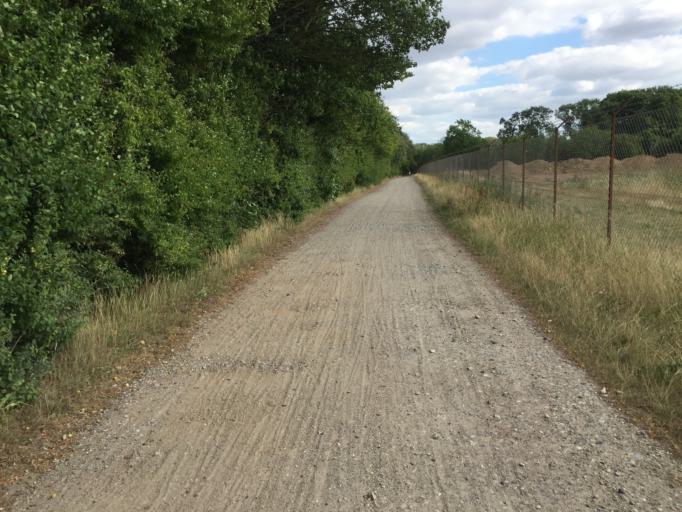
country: DK
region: South Denmark
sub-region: Odense Kommune
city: Neder Holluf
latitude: 55.3577
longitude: 10.4364
